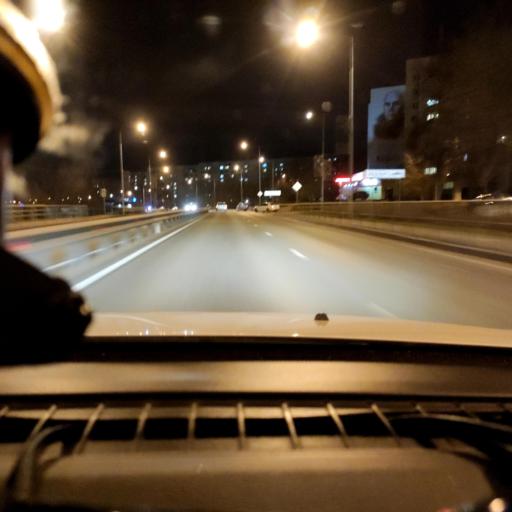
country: RU
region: Samara
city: Volzhskiy
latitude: 53.3542
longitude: 50.2110
